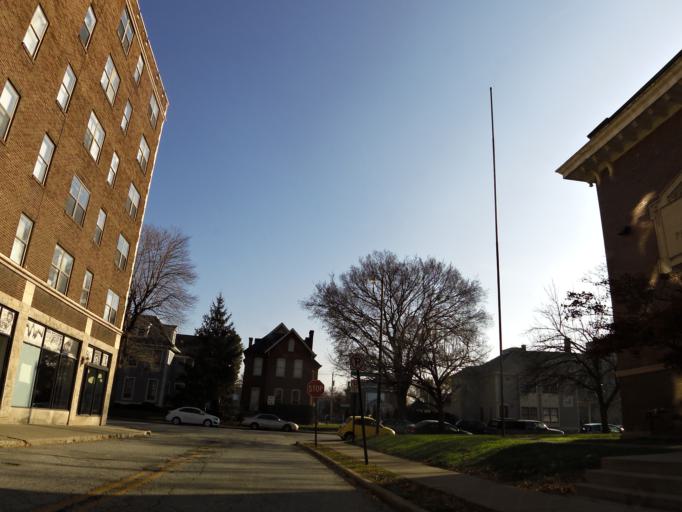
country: US
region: Indiana
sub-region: Marion County
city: Indianapolis
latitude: 39.7857
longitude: -86.1562
